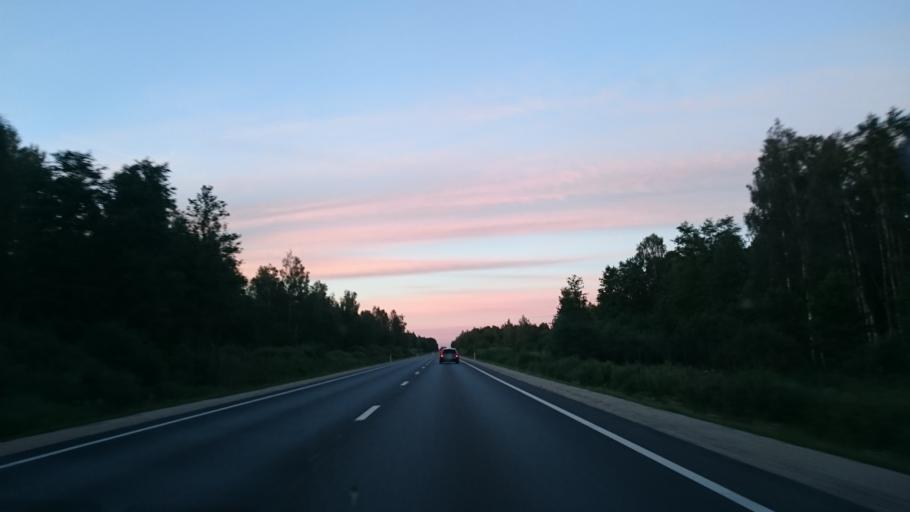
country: LV
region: Dobeles Rajons
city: Dobele
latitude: 56.7504
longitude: 23.2705
